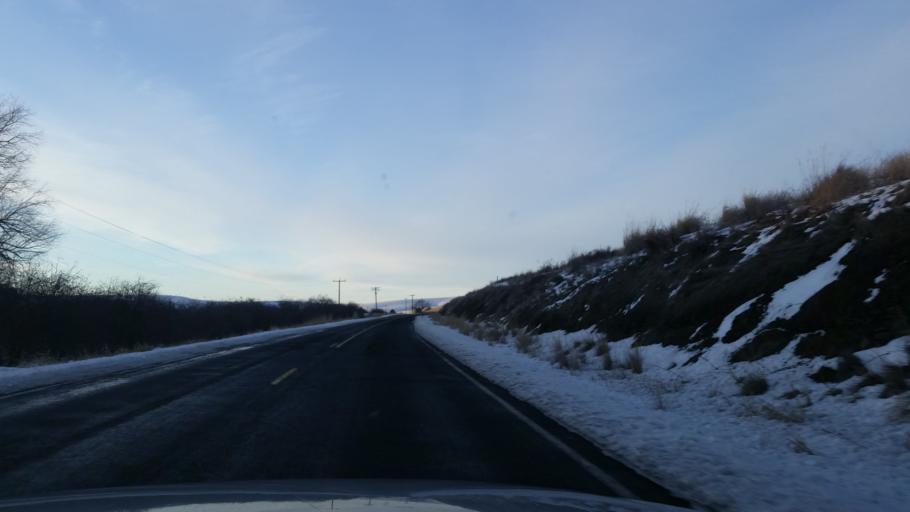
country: US
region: Washington
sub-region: Whitman County
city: Colfax
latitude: 47.1013
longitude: -117.6120
